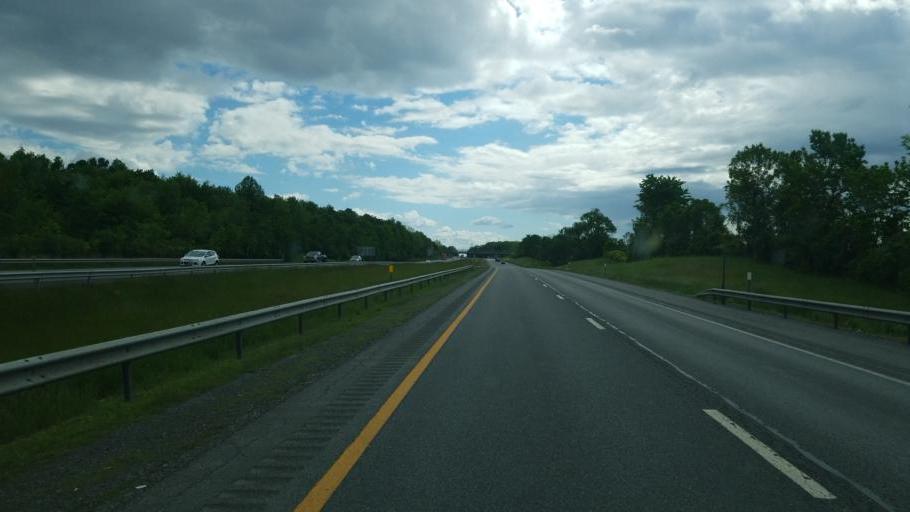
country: US
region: New York
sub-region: Seneca County
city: Seneca Falls
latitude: 42.9705
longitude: -76.8244
